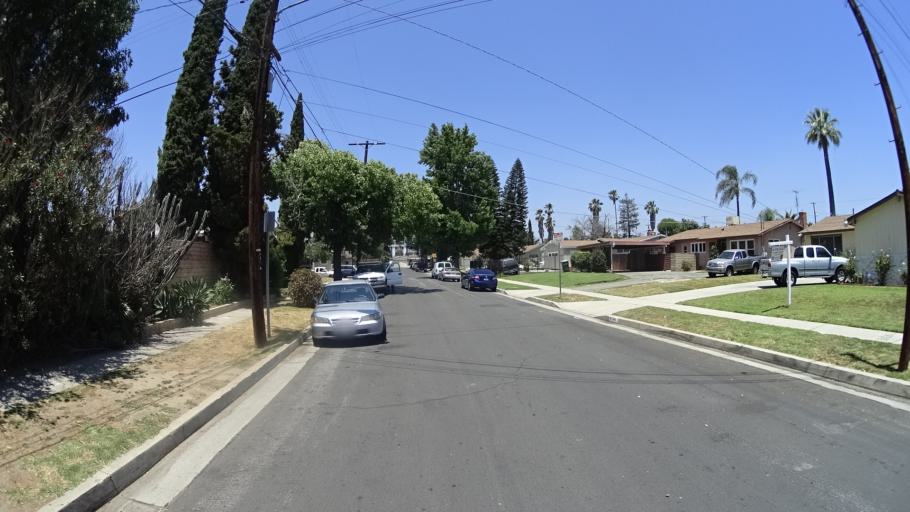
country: US
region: California
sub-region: Los Angeles County
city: Van Nuys
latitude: 34.2261
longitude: -118.4585
